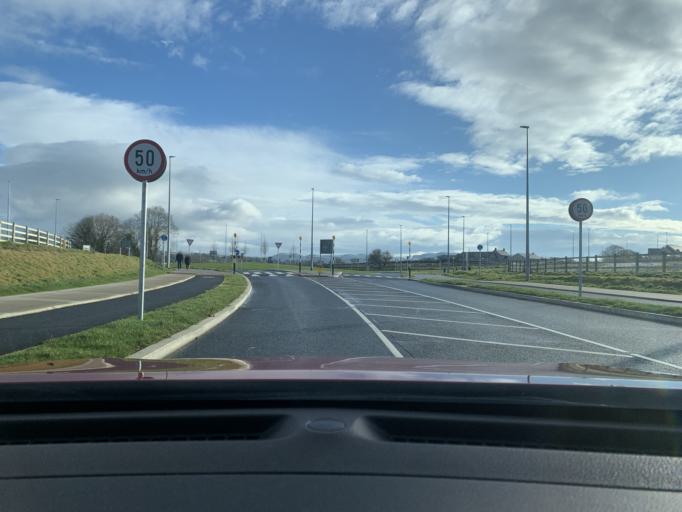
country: IE
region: Connaught
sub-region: Sligo
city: Sligo
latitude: 54.2609
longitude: -8.4998
